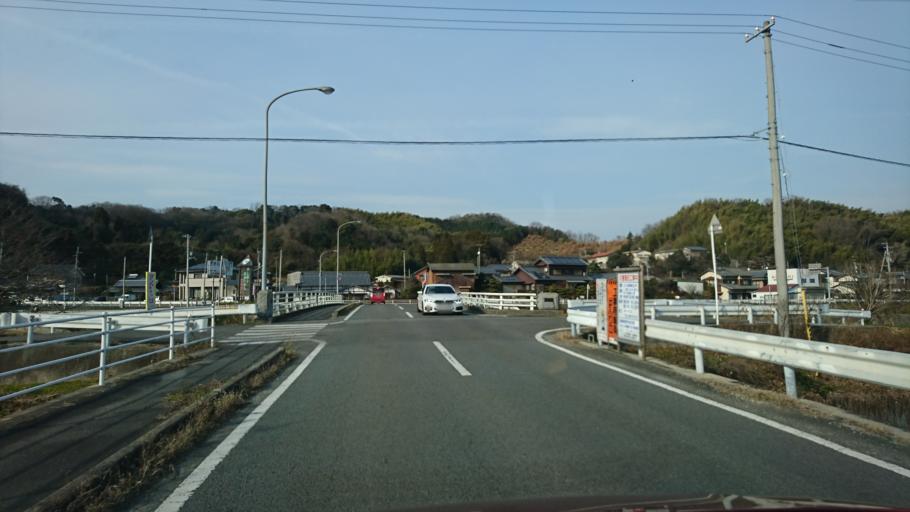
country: JP
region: Ehime
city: Hojo
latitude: 34.0267
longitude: 132.9600
